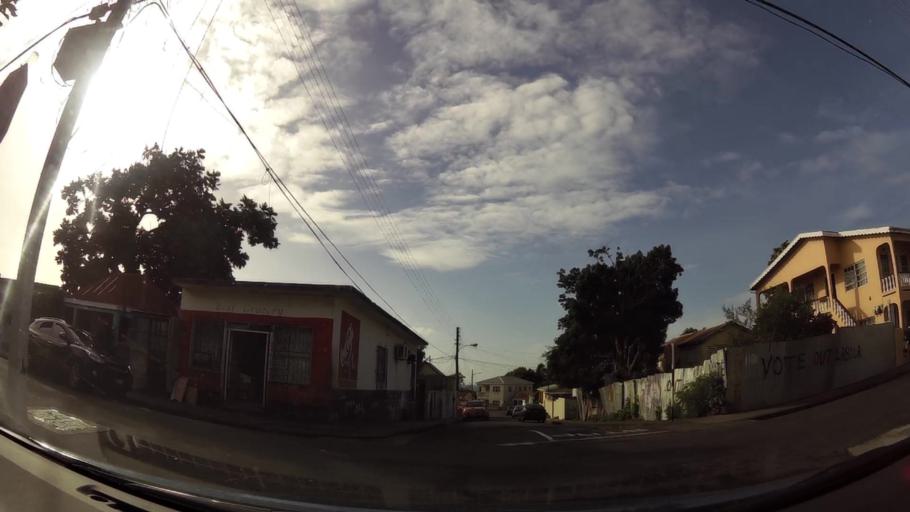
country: KN
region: Saint George Basseterre
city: Basseterre
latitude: 17.2956
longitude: -62.7301
